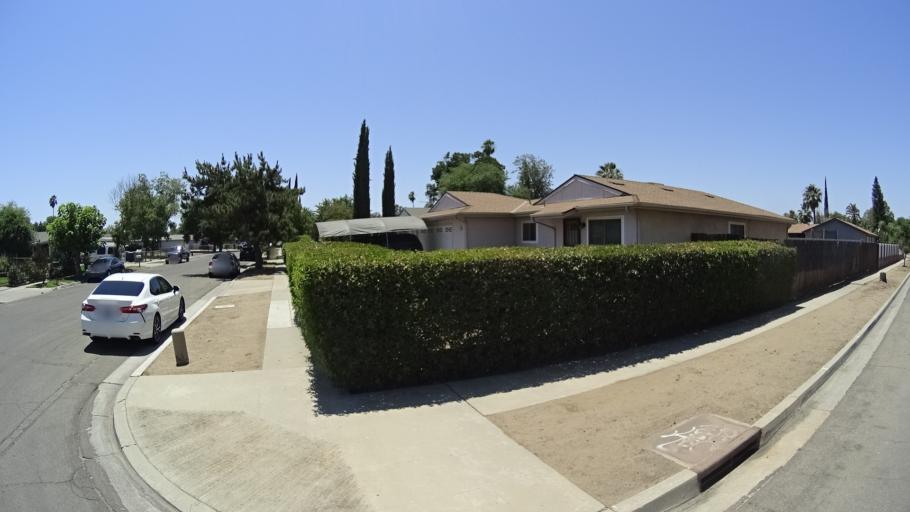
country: US
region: California
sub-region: Fresno County
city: West Park
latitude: 36.7318
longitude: -119.8288
